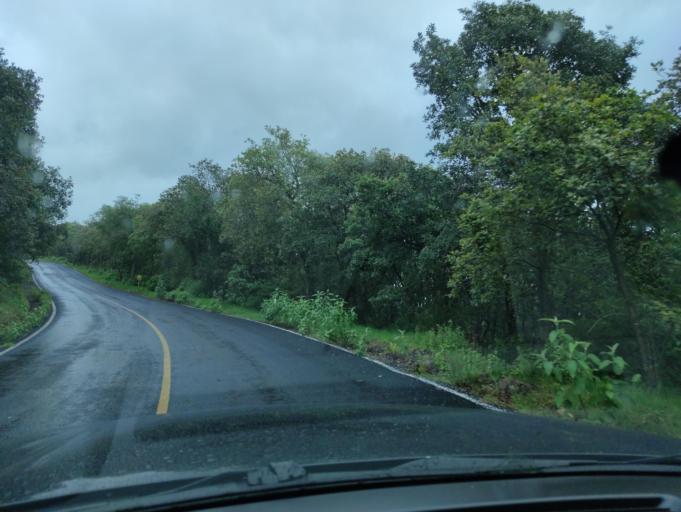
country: MX
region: Mexico
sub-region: Morelos
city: San Marcos Tlazalpan
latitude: 19.8754
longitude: -99.6591
